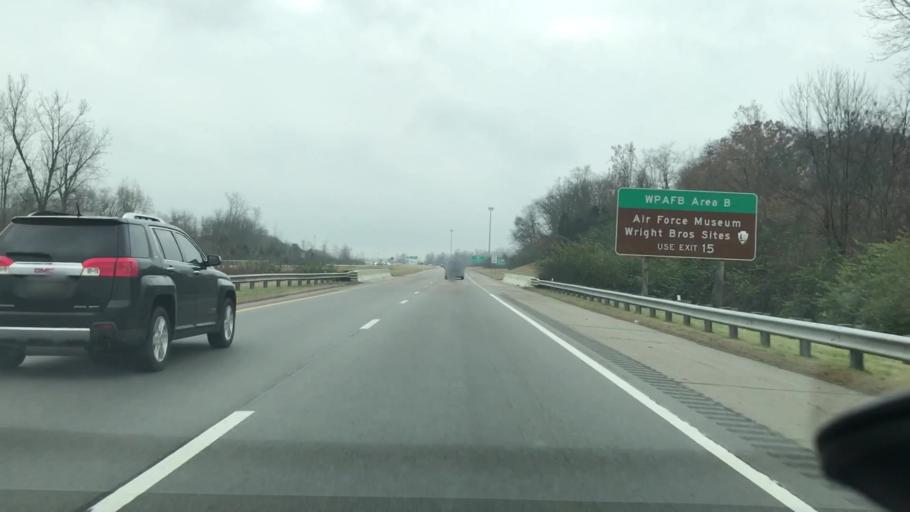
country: US
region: Ohio
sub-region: Clark County
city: Holiday Valley
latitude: 39.8564
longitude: -83.9944
